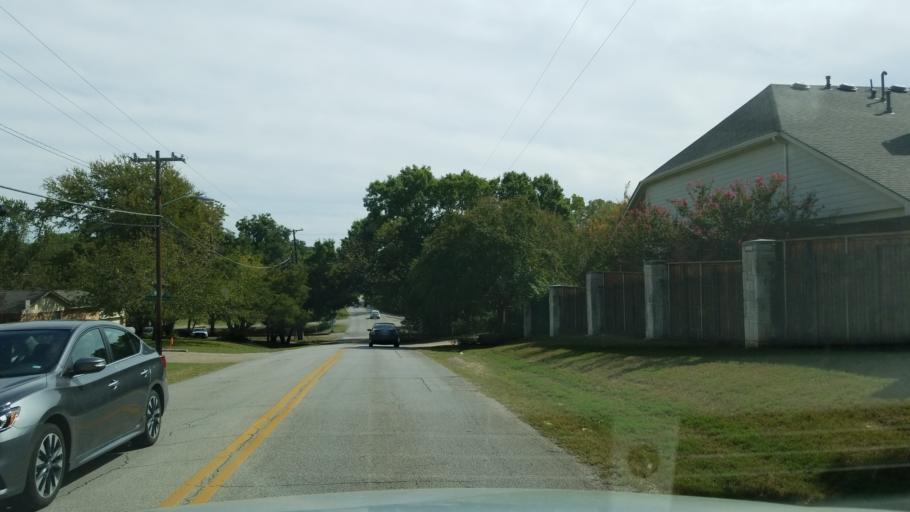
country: US
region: Texas
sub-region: Dallas County
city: Highland Park
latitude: 32.8066
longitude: -96.7196
